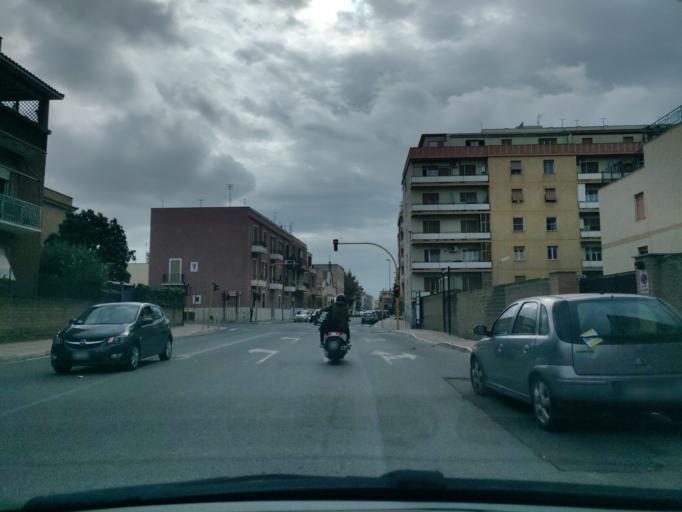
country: IT
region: Latium
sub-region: Citta metropolitana di Roma Capitale
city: Civitavecchia
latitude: 42.0965
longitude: 11.8024
